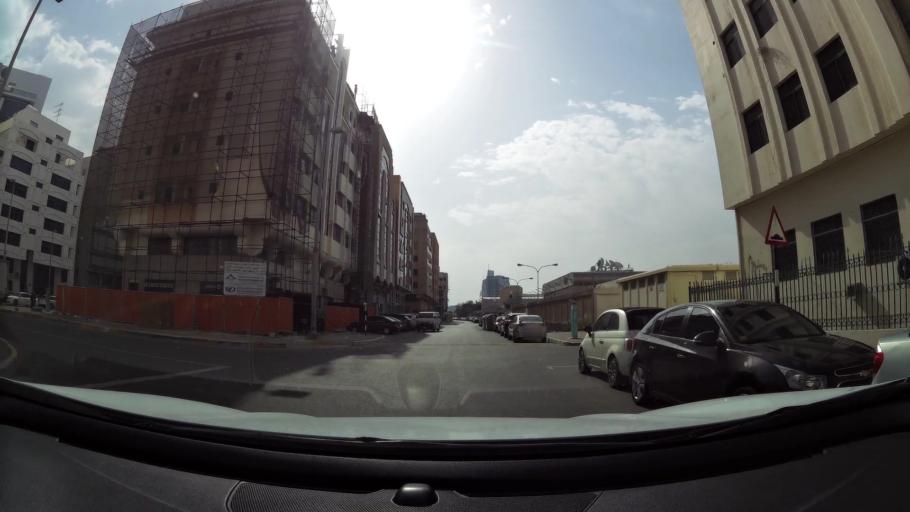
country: AE
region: Abu Dhabi
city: Abu Dhabi
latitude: 24.4589
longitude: 54.3879
